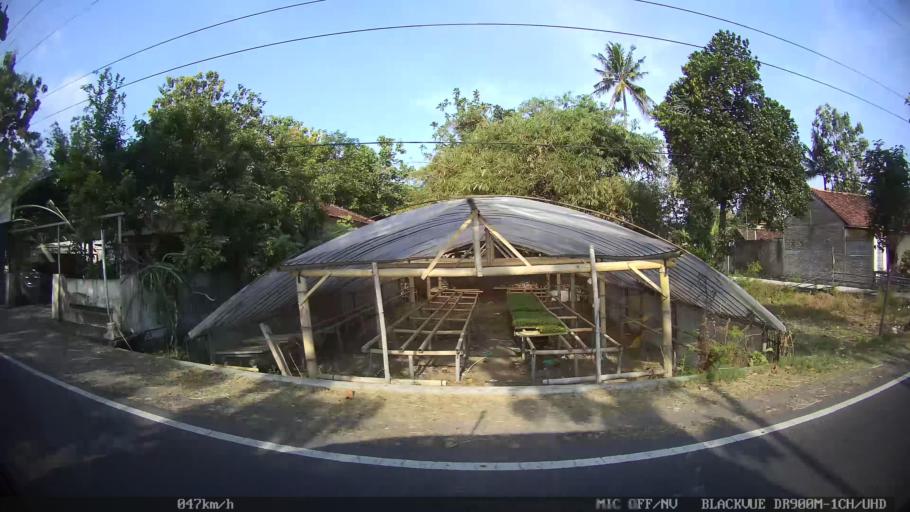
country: ID
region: Daerah Istimewa Yogyakarta
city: Bantul
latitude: -7.8871
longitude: 110.3179
